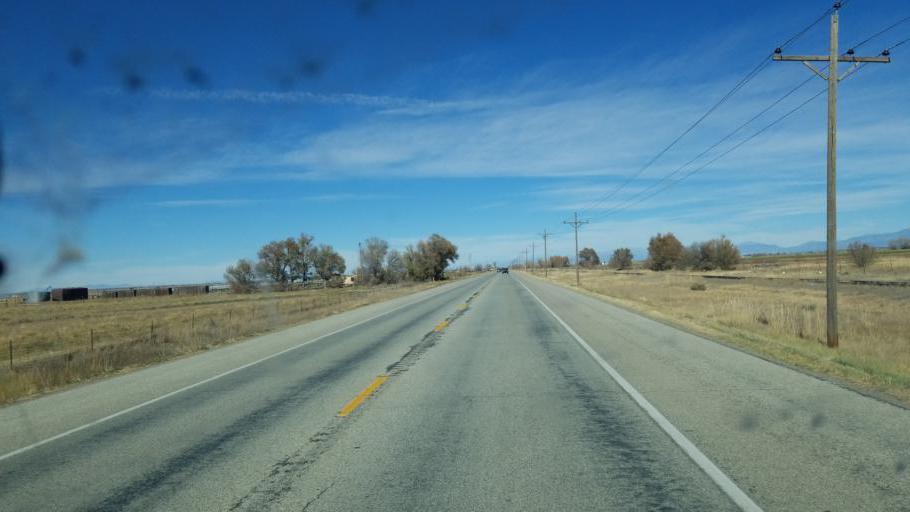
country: US
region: Colorado
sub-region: Conejos County
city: Conejos
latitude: 37.1869
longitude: -105.9841
